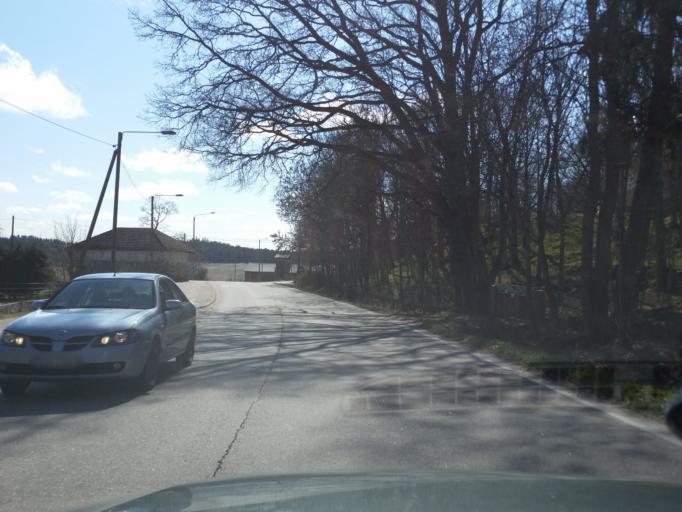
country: FI
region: Uusimaa
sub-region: Helsinki
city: Vihti
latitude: 60.4192
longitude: 24.2959
